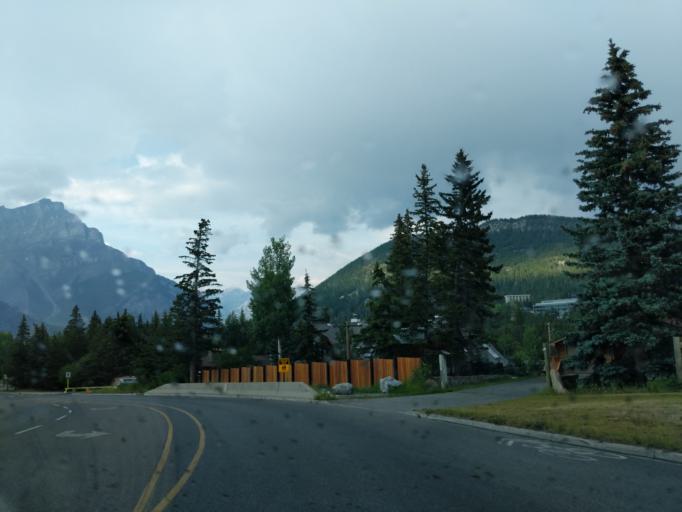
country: CA
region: Alberta
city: Banff
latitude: 51.1687
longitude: -115.5705
